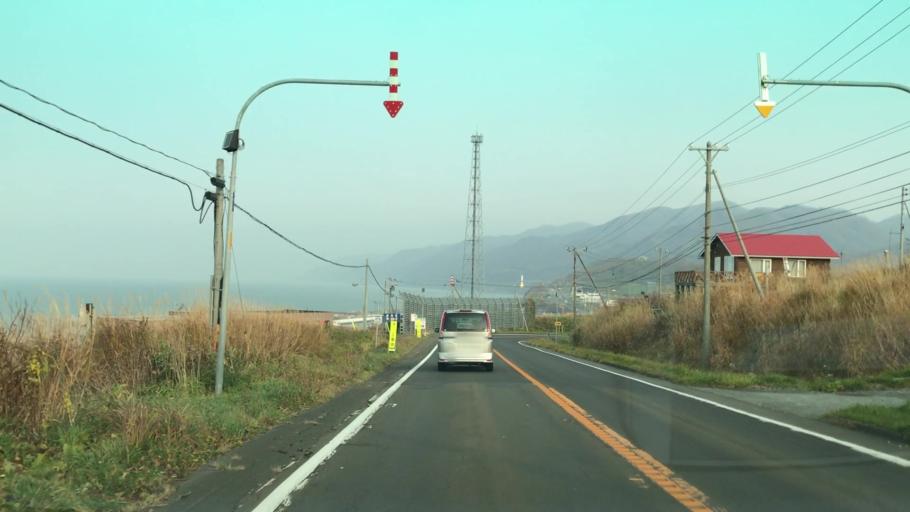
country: JP
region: Hokkaido
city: Ishikari
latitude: 43.3925
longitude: 141.4327
